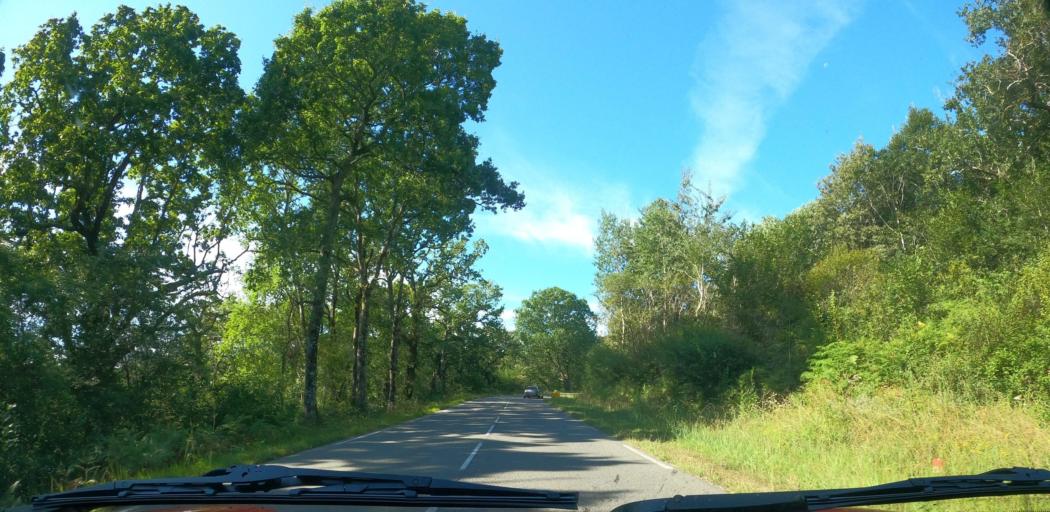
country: FR
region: Aquitaine
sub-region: Departement des Pyrenees-Atlantiques
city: Saint-Pee-sur-Nivelle
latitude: 43.3863
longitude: -1.5404
